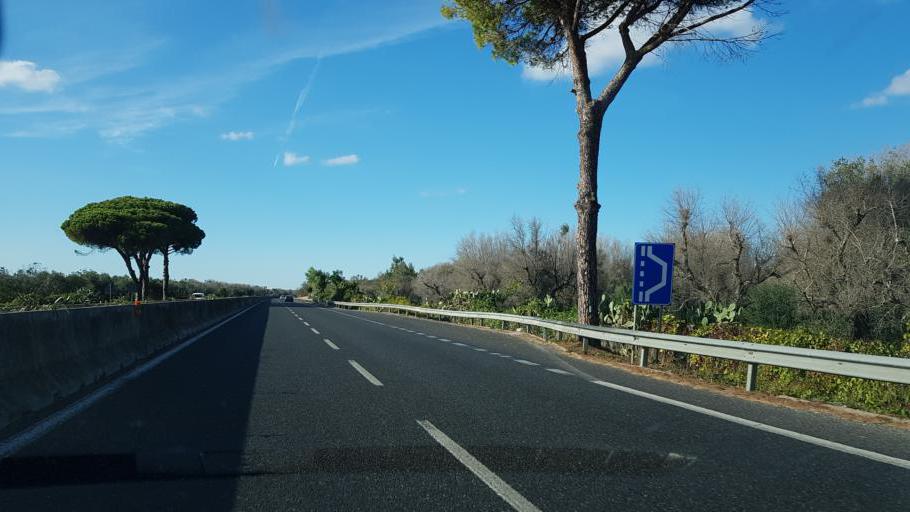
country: IT
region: Apulia
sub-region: Provincia di Brindisi
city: Torchiarolo
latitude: 40.4646
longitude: 18.0562
